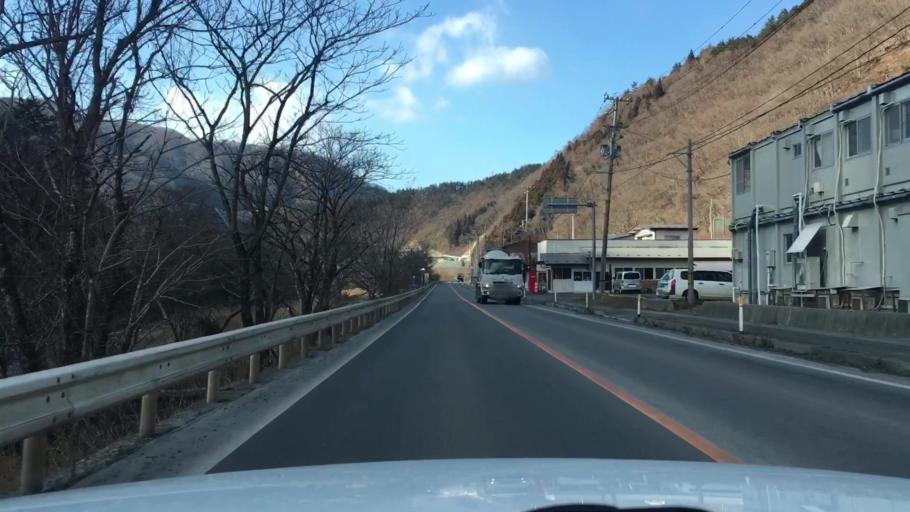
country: JP
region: Iwate
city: Miyako
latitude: 39.5927
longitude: 141.6642
